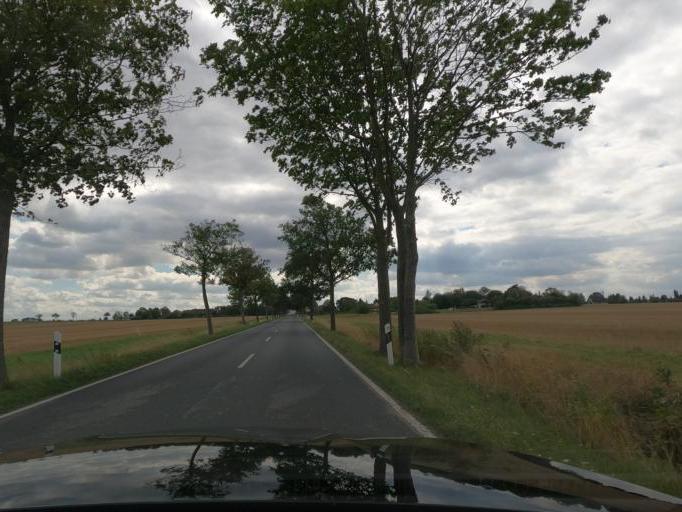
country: DE
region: Lower Saxony
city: Sehnde
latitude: 52.3223
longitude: 10.0254
